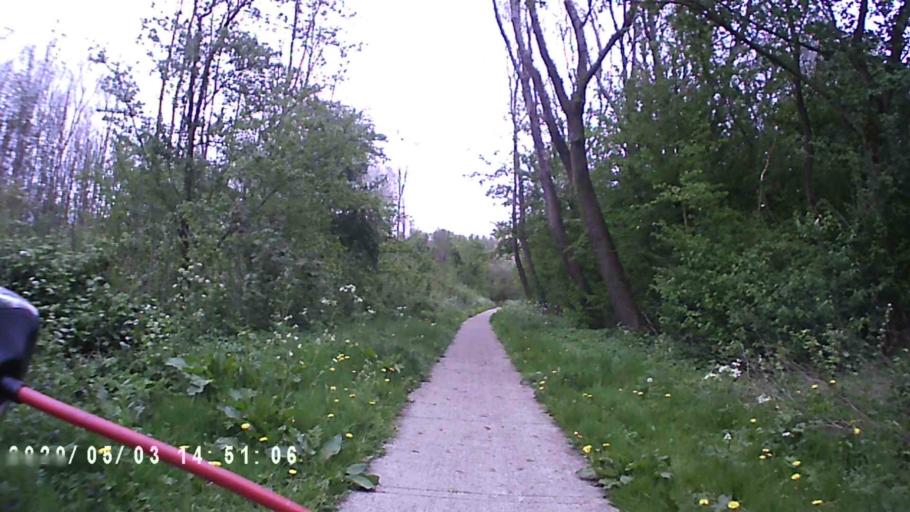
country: NL
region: Groningen
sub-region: Gemeente Zuidhorn
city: Oldehove
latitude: 53.3625
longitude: 6.4187
